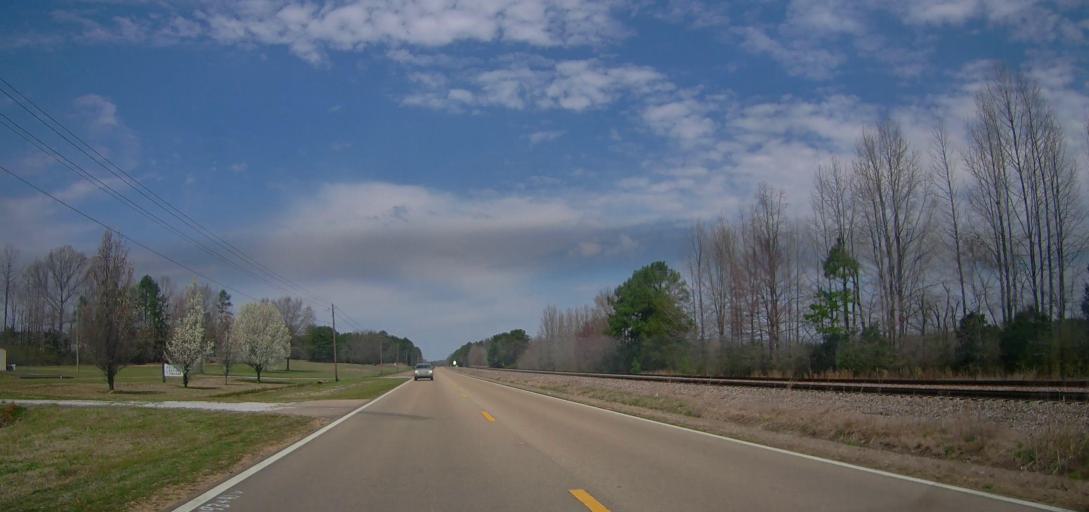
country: US
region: Mississippi
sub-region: Union County
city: New Albany
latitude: 34.5797
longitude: -89.1309
